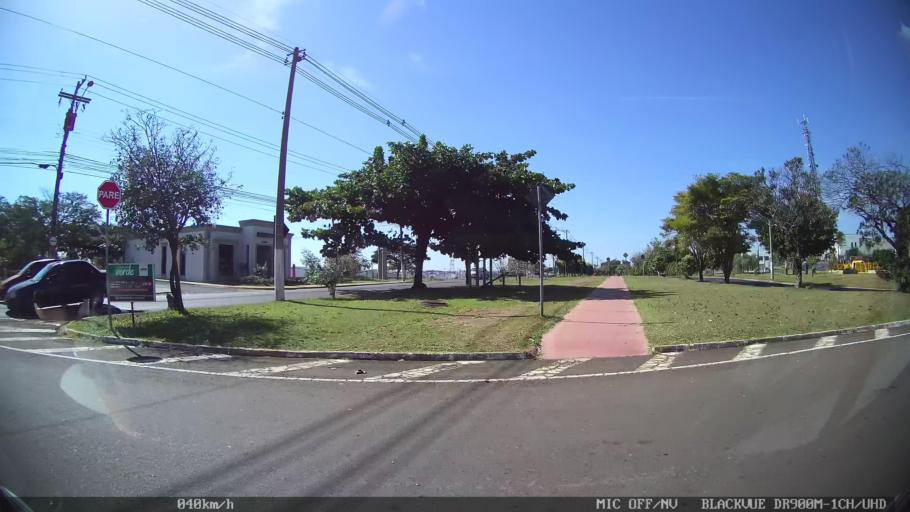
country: BR
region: Sao Paulo
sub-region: Franca
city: Franca
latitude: -20.5480
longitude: -47.4369
